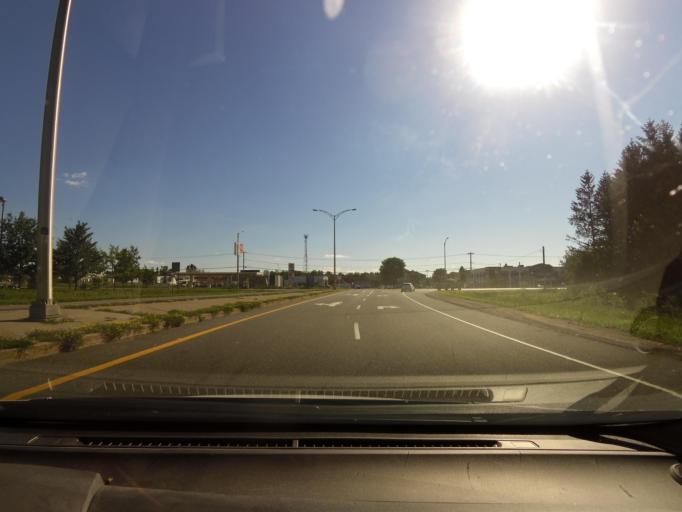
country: CA
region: Quebec
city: Sainte-Catherine
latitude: 46.2933
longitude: -72.5398
